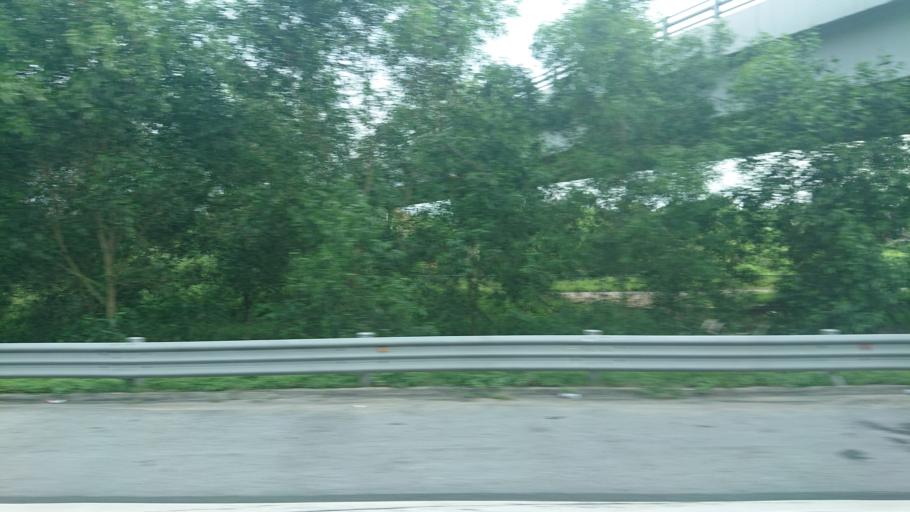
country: VN
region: Hai Phong
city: An Lao
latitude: 20.7874
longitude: 106.5581
